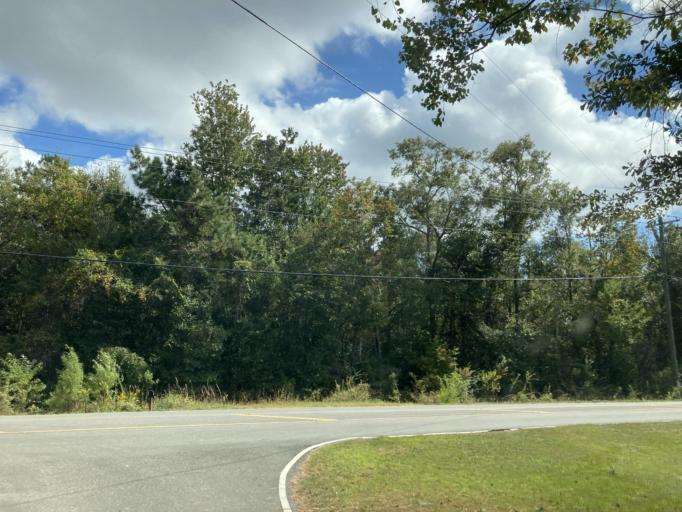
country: US
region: Mississippi
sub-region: Jackson County
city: Gulf Hills
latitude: 30.4497
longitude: -88.8306
